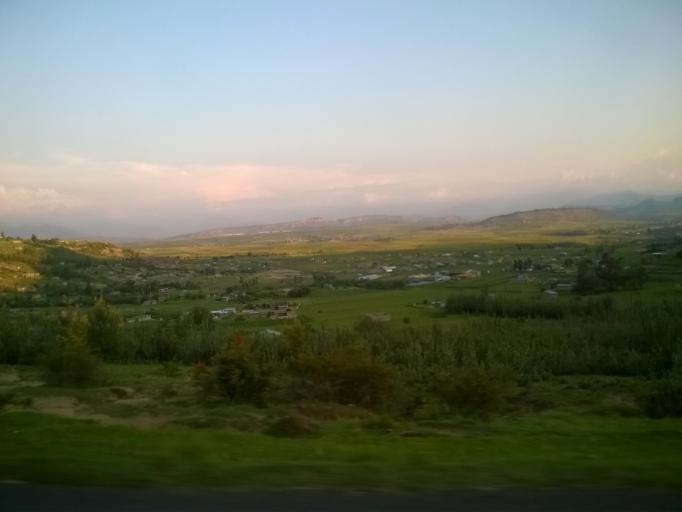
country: LS
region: Leribe
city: Leribe
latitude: -28.8872
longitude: 28.1027
